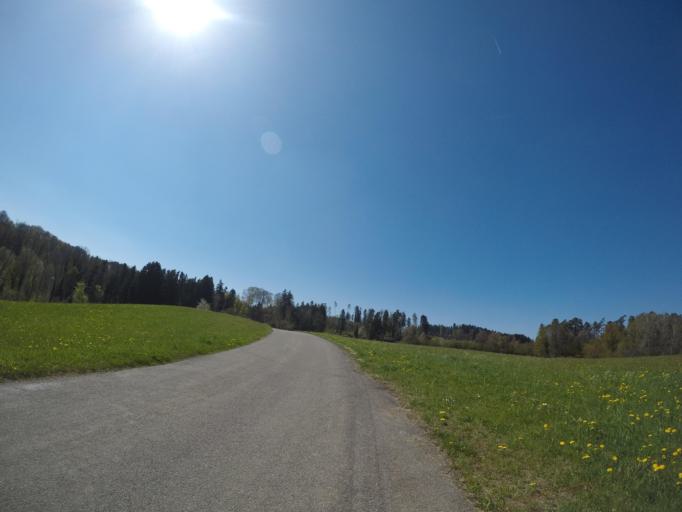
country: DE
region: Baden-Wuerttemberg
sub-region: Tuebingen Region
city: Markdorf
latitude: 47.7654
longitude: 9.4027
